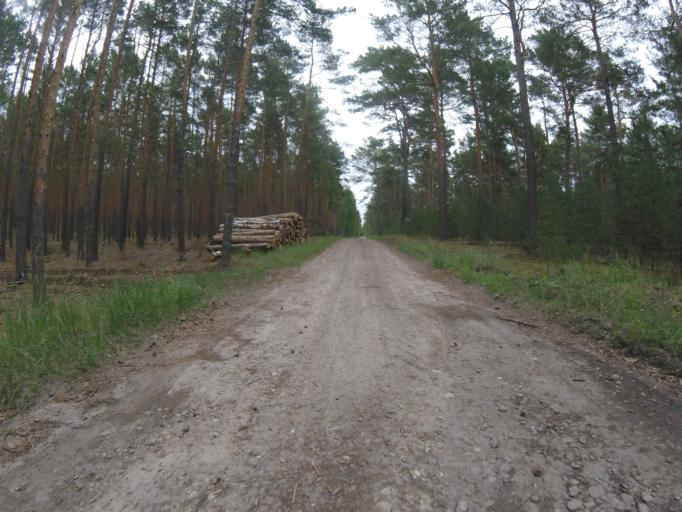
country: DE
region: Brandenburg
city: Gross Koris
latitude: 52.1935
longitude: 13.6859
